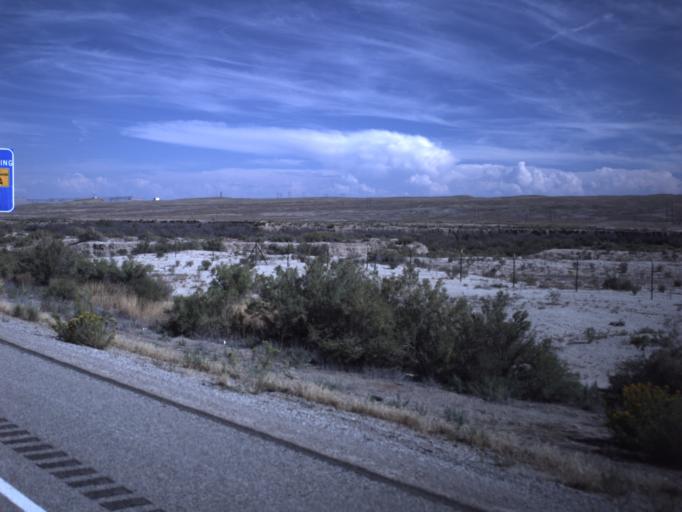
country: US
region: Utah
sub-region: Carbon County
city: East Carbon City
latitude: 38.9886
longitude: -110.1993
